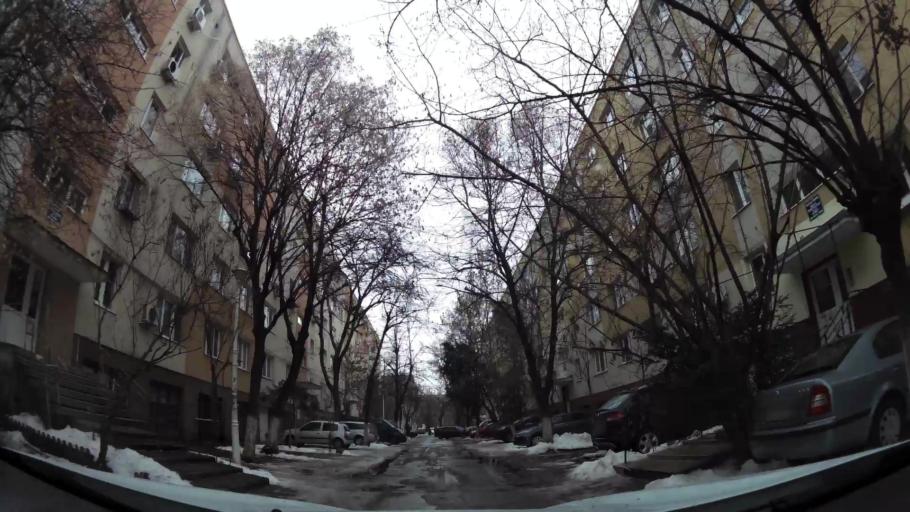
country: RO
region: Ilfov
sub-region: Comuna Chiajna
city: Rosu
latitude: 44.4195
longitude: 26.0223
